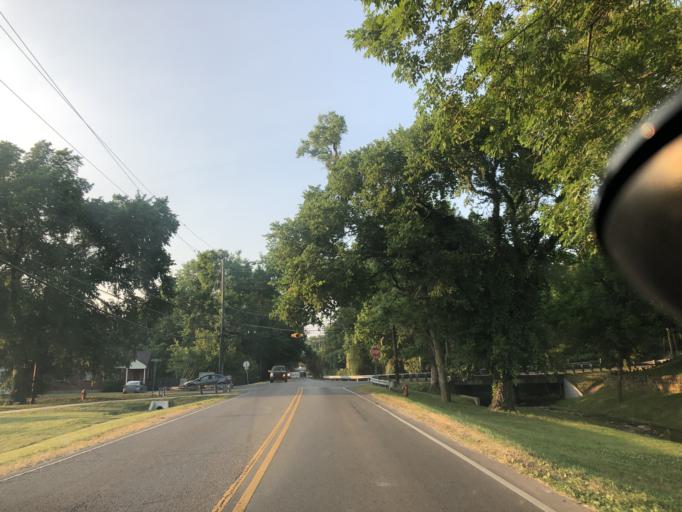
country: US
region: Tennessee
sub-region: Davidson County
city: Oak Hill
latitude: 36.1054
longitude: -86.7893
